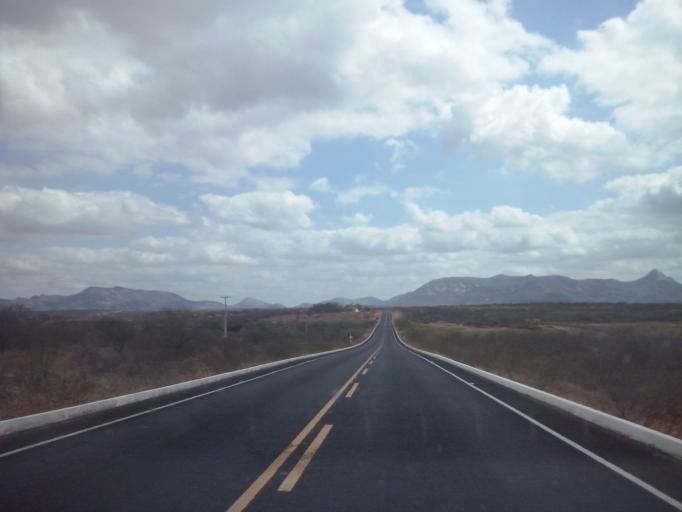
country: BR
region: Paraiba
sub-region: Pombal
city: Pombal
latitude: -6.8364
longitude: -37.5692
